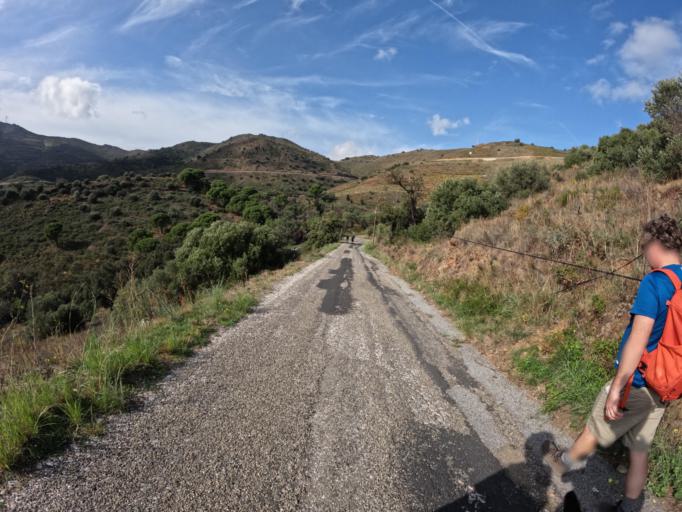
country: FR
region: Languedoc-Roussillon
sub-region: Departement des Pyrenees-Orientales
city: Cervera de la Marenda
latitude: 42.4626
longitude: 3.1556
